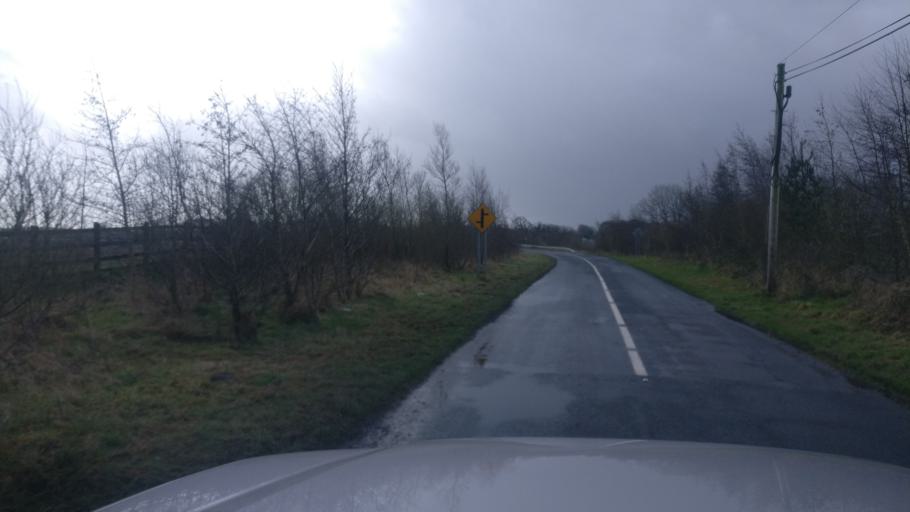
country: IE
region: Connaught
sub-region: County Galway
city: Loughrea
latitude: 53.2890
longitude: -8.4760
